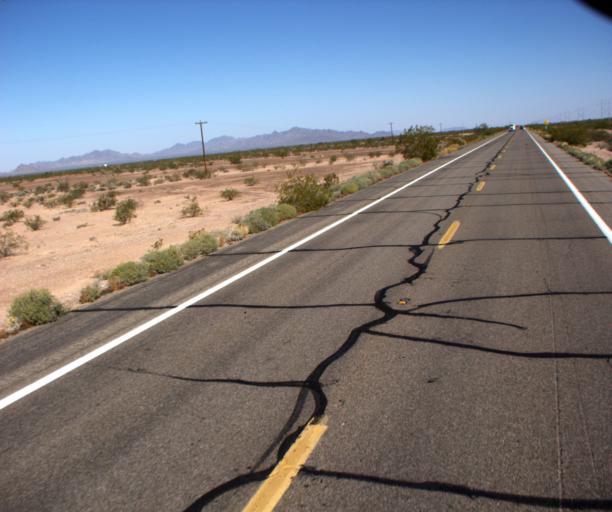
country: US
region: Arizona
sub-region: La Paz County
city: Quartzsite
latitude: 33.3529
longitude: -114.2171
